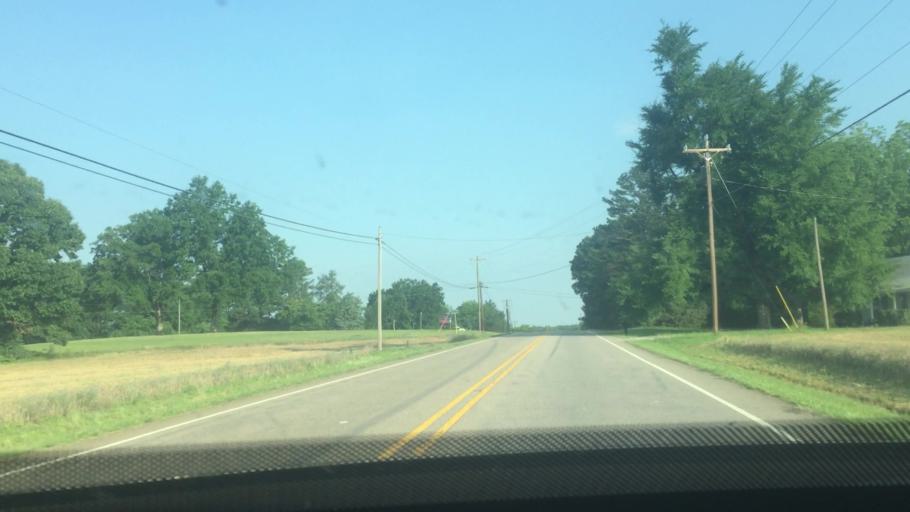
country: US
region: North Carolina
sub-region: Rowan County
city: Enochville
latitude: 35.5785
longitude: -80.7141
